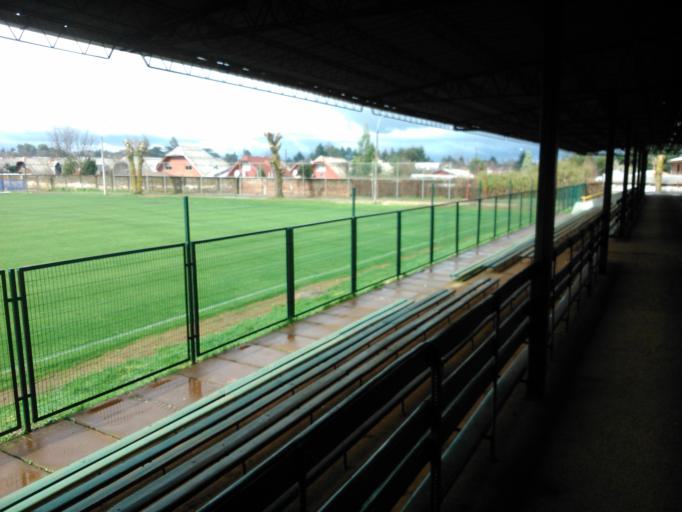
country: CL
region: Araucania
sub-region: Provincia de Cautin
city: Temuco
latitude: -38.7432
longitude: -72.6220
